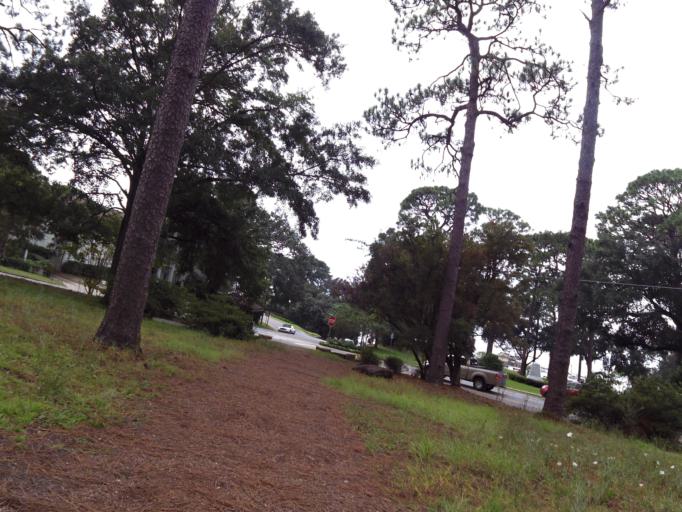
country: US
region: Alabama
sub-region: Baldwin County
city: Fairhope
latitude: 30.5239
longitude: -87.9098
